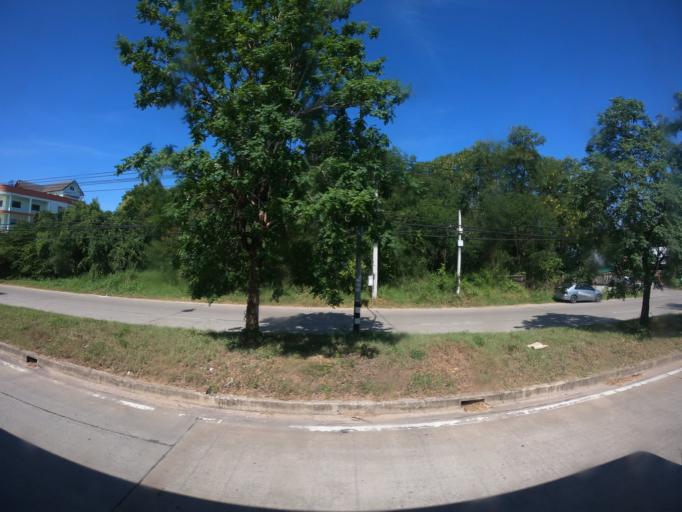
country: TH
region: Nakhon Ratchasima
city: Nakhon Ratchasima
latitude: 15.0151
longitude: 102.1291
